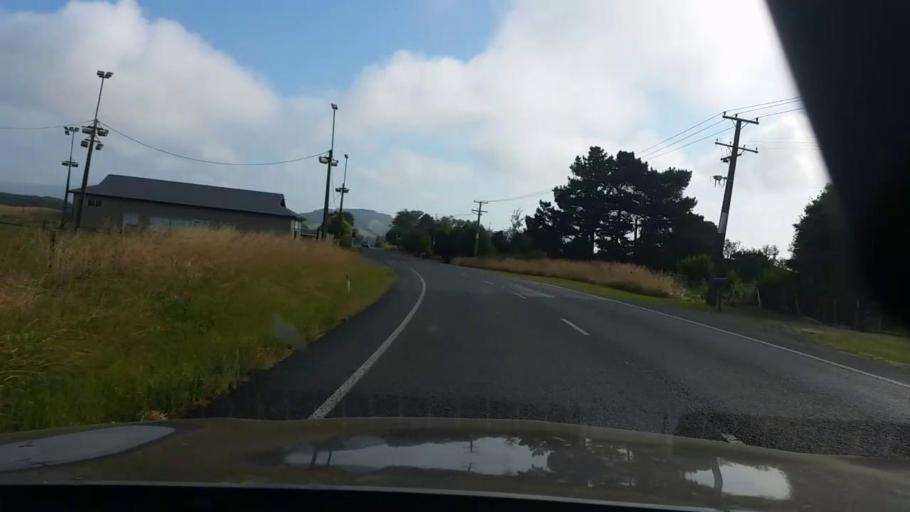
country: NZ
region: Waikato
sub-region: Hamilton City
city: Hamilton
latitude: -37.6144
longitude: 175.3443
